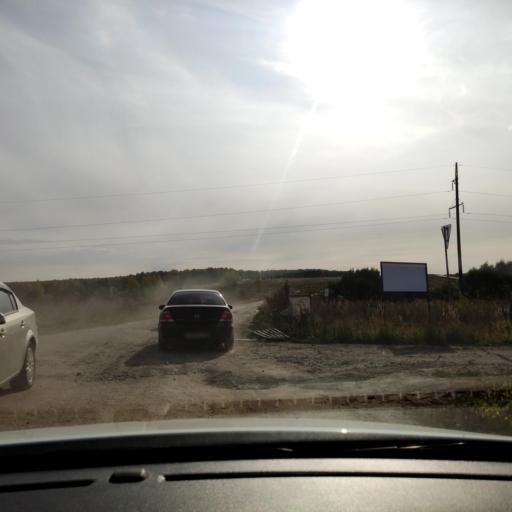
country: RU
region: Tatarstan
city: Vysokaya Gora
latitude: 55.8639
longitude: 49.3660
